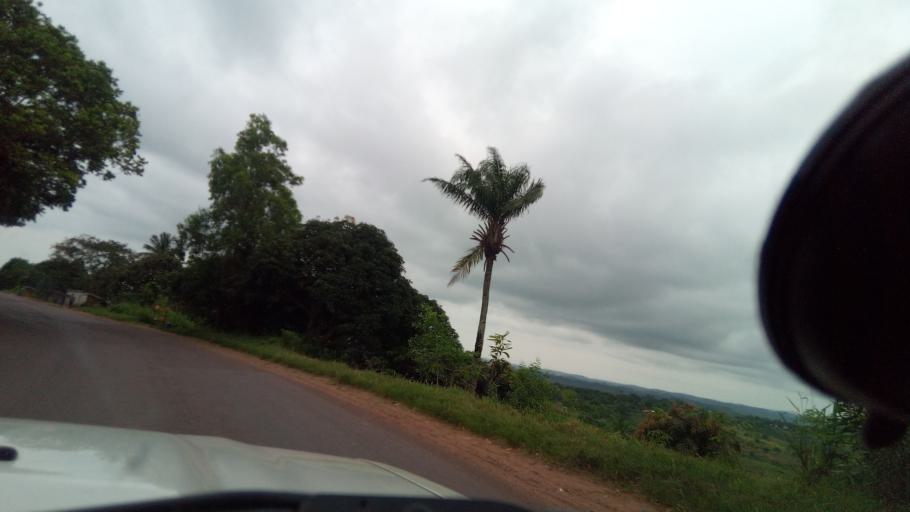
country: CD
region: Bas-Congo
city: Kasangulu
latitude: -4.9058
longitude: 15.1623
